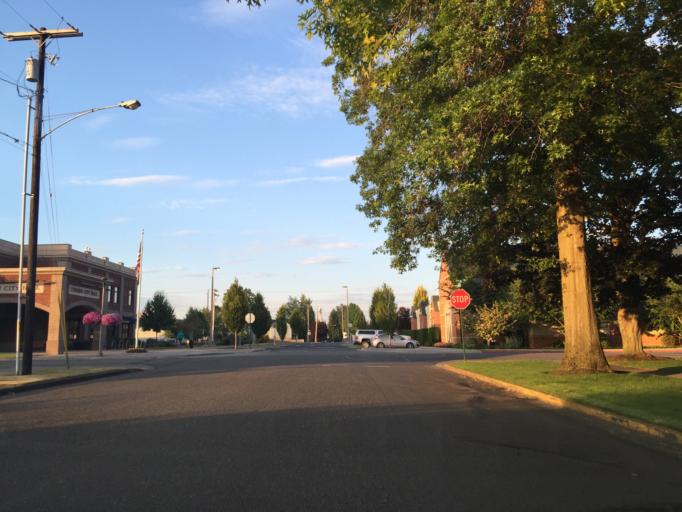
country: US
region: Washington
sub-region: Whatcom County
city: Lynden
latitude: 48.9449
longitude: -122.4536
